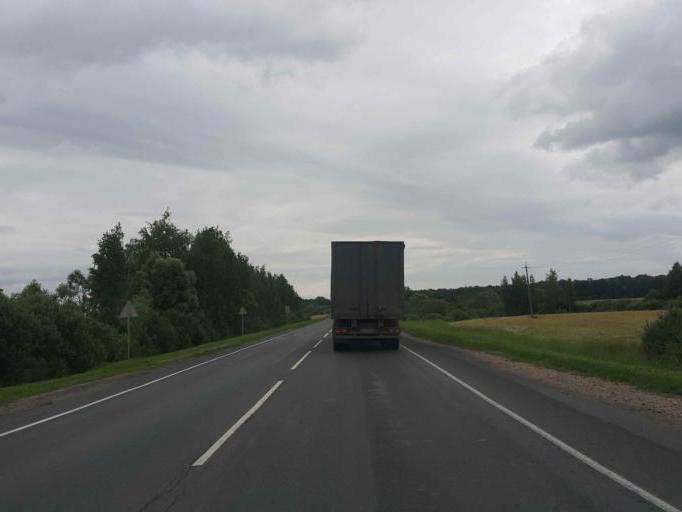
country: RU
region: Tambov
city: Zavoronezhskoye
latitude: 52.9249
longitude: 40.6189
